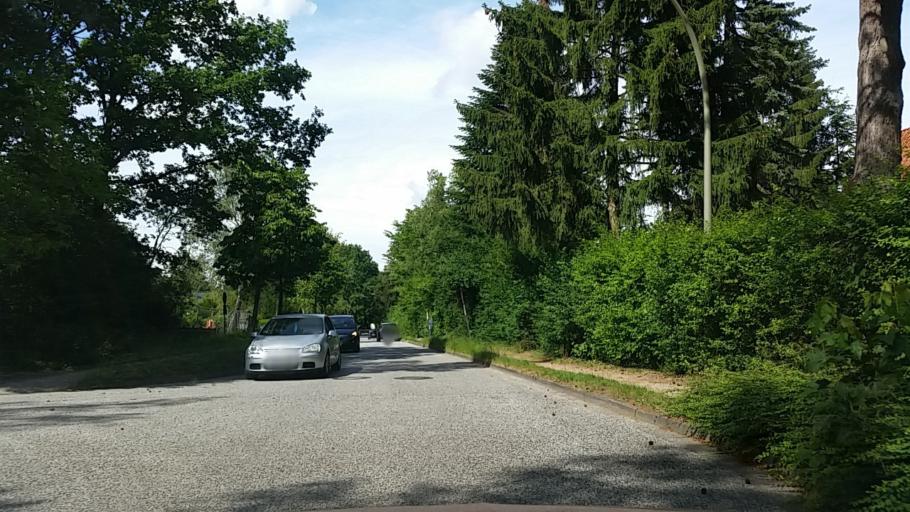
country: DE
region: Schleswig-Holstein
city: Wedel
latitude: 53.5876
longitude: 9.7639
